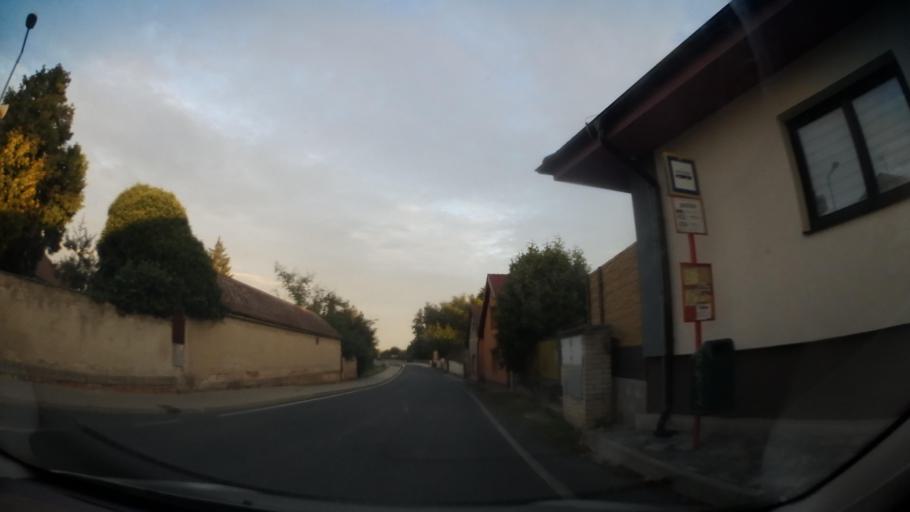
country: CZ
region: Central Bohemia
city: Milovice
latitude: 50.2269
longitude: 14.9378
